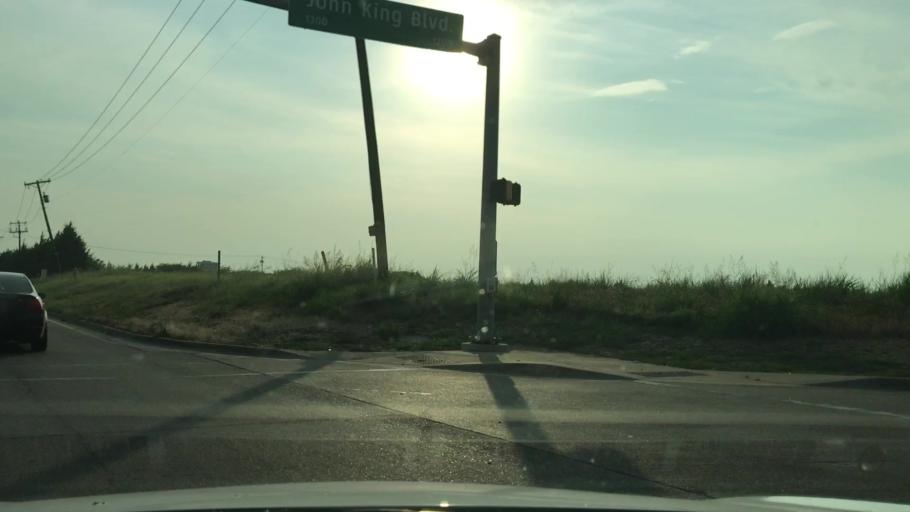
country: US
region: Texas
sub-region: Rockwall County
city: Rockwall
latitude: 32.9165
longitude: -96.4330
